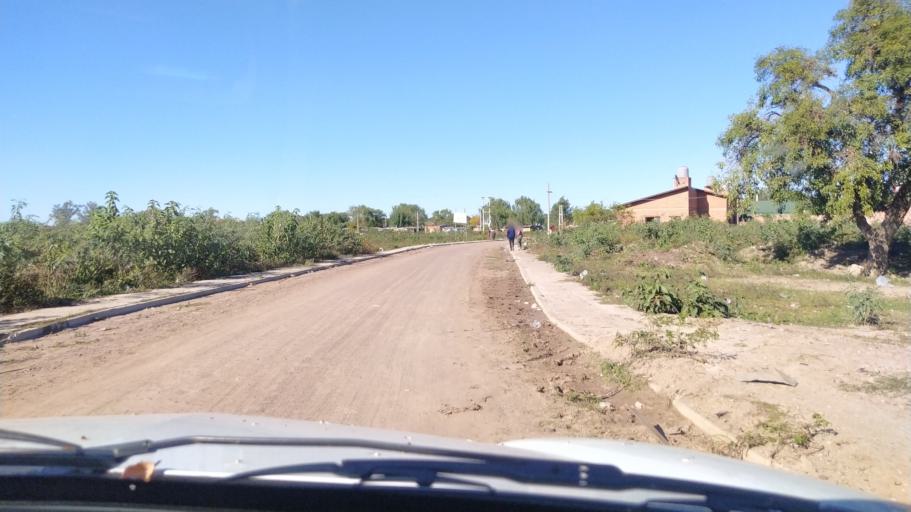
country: AR
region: Corrientes
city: Corrientes
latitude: -27.4978
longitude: -58.8036
